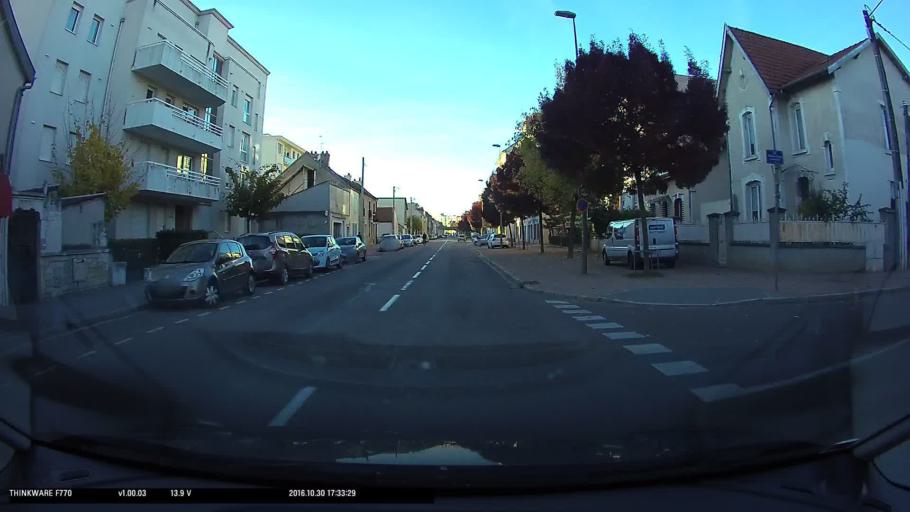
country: FR
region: Bourgogne
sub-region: Departement de la Cote-d'Or
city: Longvic
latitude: 47.3090
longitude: 5.0555
